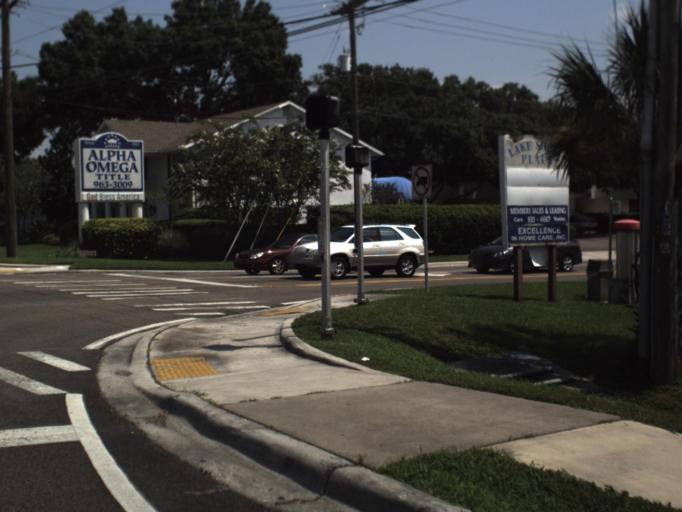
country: US
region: Florida
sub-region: Hillsborough County
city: Carrollwood Village
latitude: 28.0747
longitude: -82.5067
